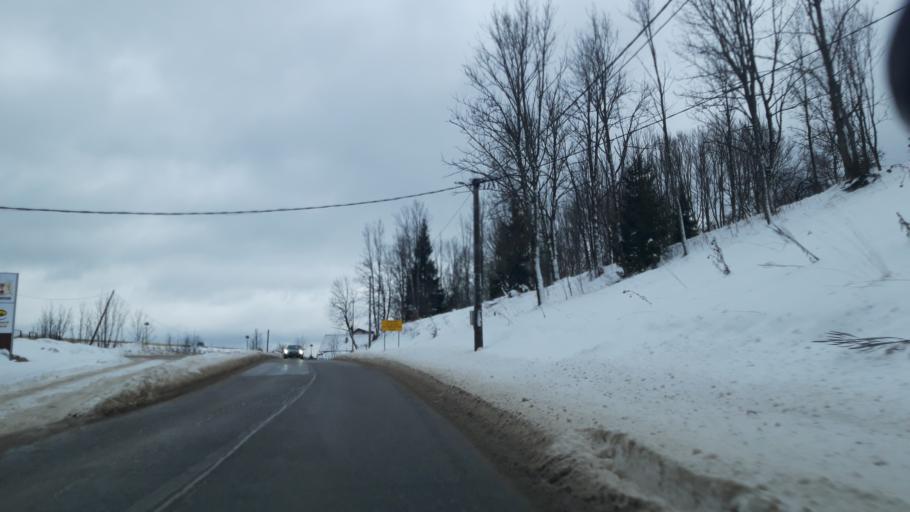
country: BA
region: Republika Srpska
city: Han Pijesak
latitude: 44.0853
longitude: 18.9538
